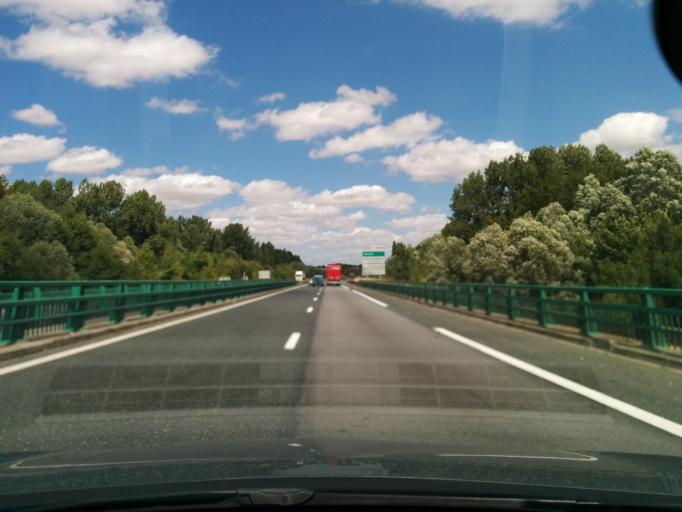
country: FR
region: Centre
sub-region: Departement de l'Indre
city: Saint-Maur
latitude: 46.8143
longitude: 1.6211
